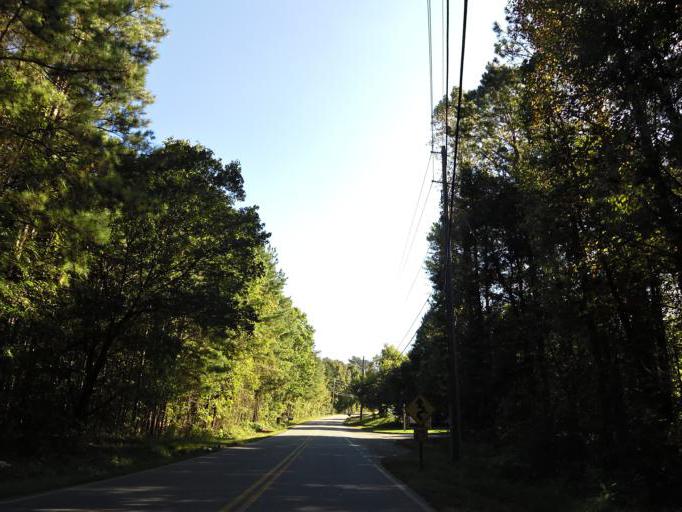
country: US
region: Georgia
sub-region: Cobb County
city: Acworth
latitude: 34.1224
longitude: -84.6800
